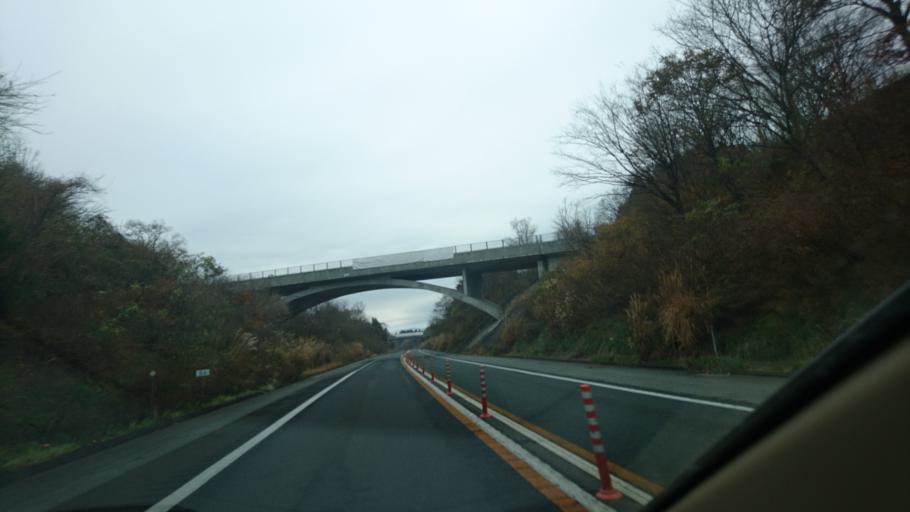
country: JP
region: Iwate
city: Kitakami
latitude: 39.2799
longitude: 141.0162
